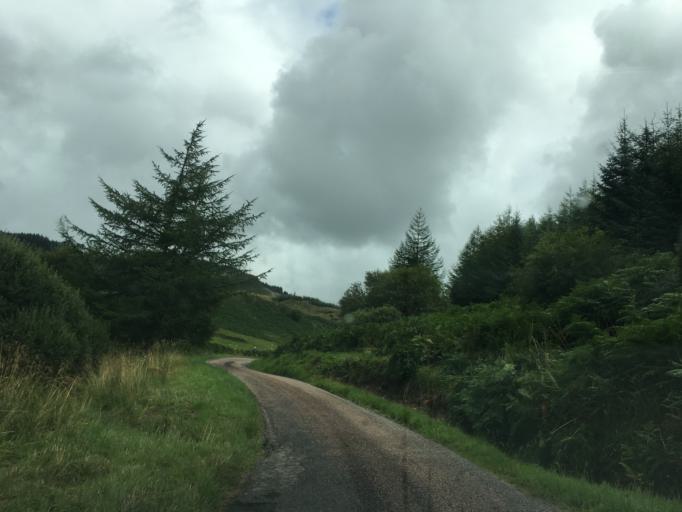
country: GB
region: Scotland
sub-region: Argyll and Bute
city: Oban
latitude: 56.2565
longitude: -5.4018
